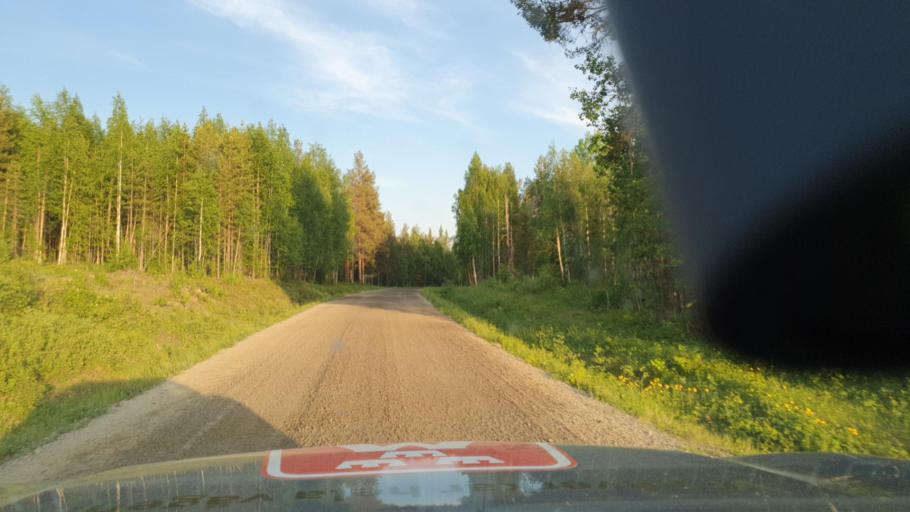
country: SE
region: Norrbotten
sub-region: Bodens Kommun
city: Boden
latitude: 66.1922
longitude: 21.4999
